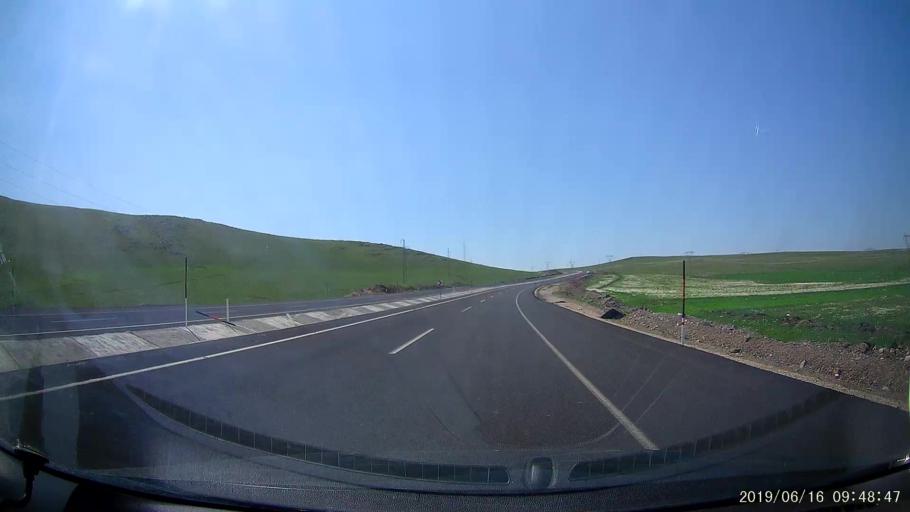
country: TR
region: Kars
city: Digor
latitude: 40.4297
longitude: 43.3557
